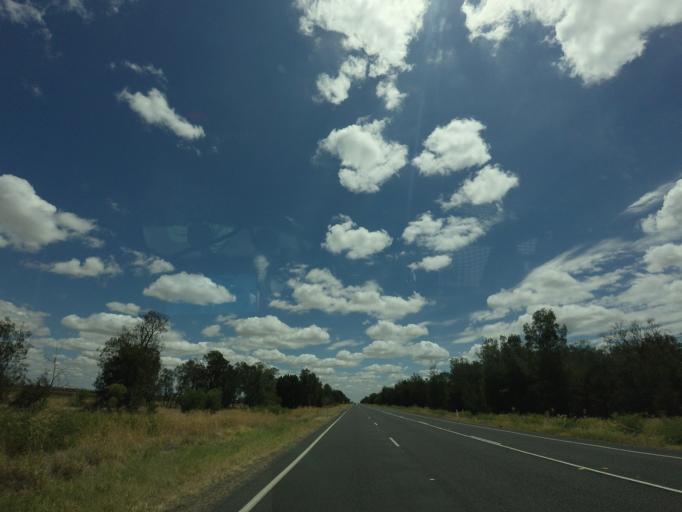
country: AU
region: New South Wales
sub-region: Moree Plains
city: Boggabilla
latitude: -28.9745
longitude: 150.0803
